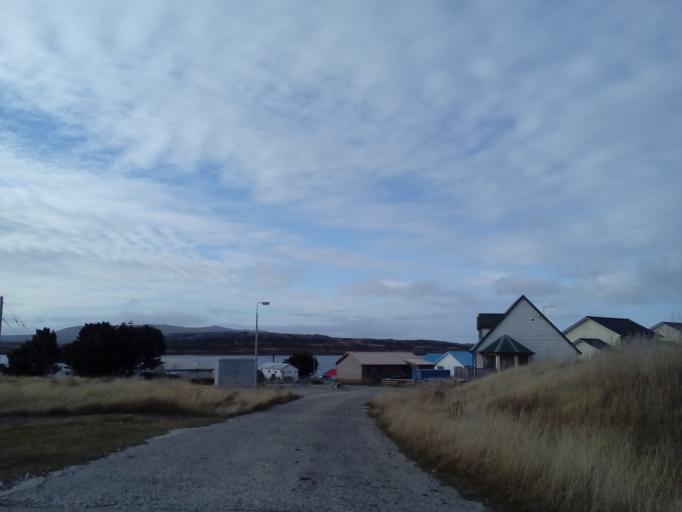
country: FK
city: Stanley
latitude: -51.6923
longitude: -57.8766
